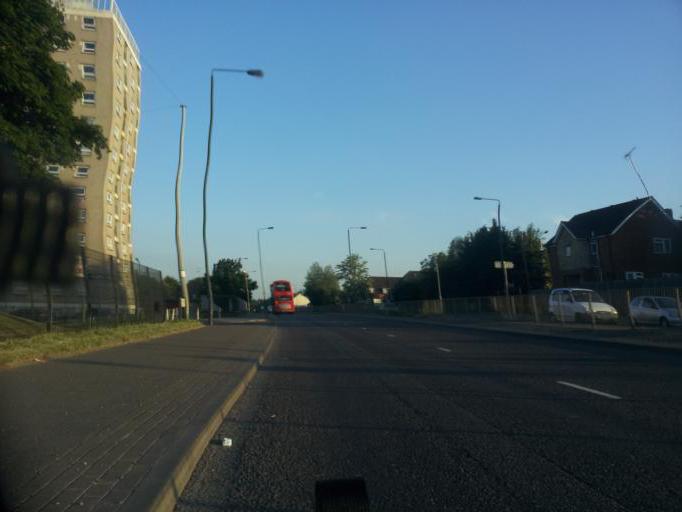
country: GB
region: England
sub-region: Greater London
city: Erith
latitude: 51.4710
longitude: 0.1810
